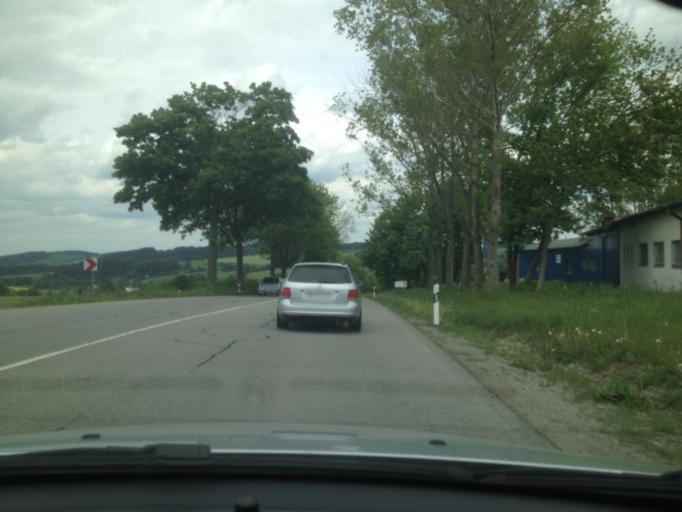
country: DE
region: Saxony
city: Schlettau
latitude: 50.5514
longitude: 12.9429
